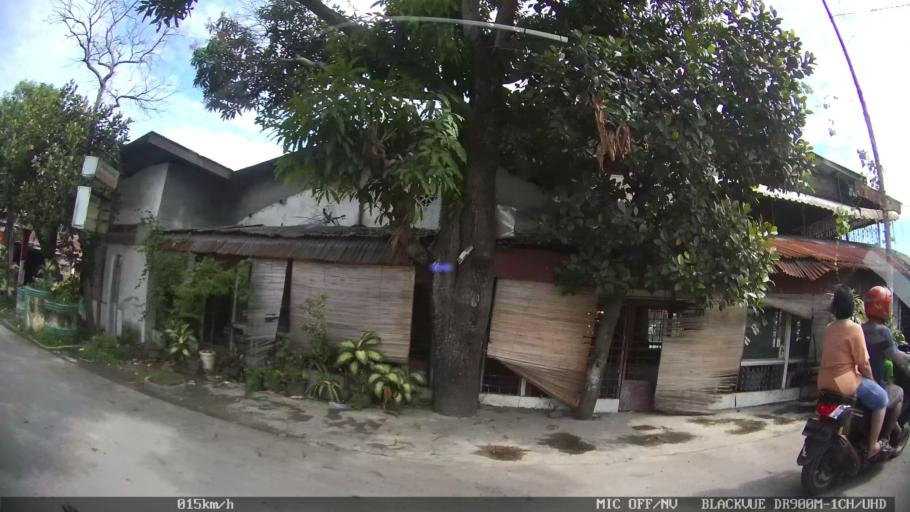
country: ID
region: North Sumatra
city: Medan
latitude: 3.6233
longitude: 98.6721
